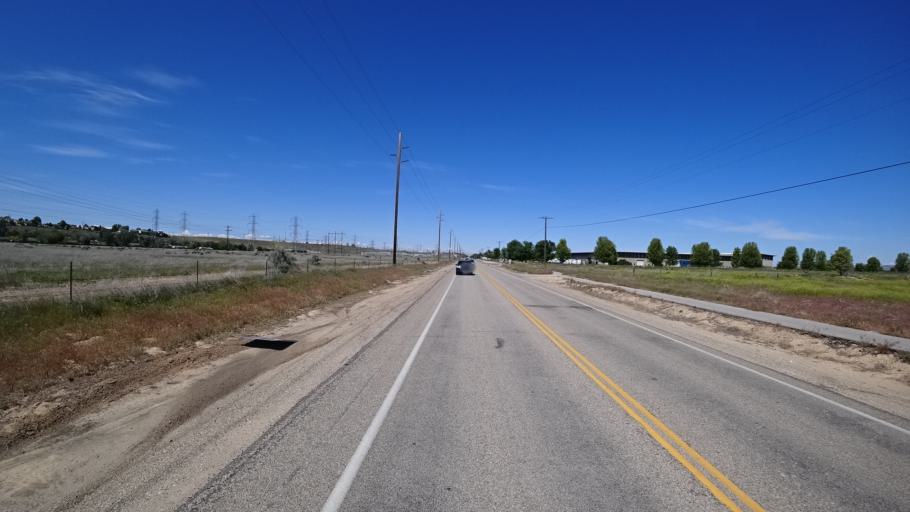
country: US
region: Idaho
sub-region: Ada County
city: Boise
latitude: 43.5600
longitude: -116.1454
